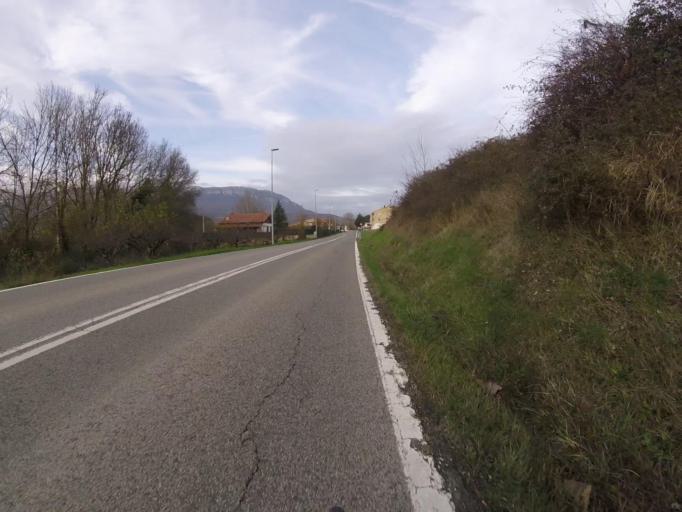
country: ES
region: Navarre
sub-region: Provincia de Navarra
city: Estella
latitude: 42.7081
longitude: -2.0696
